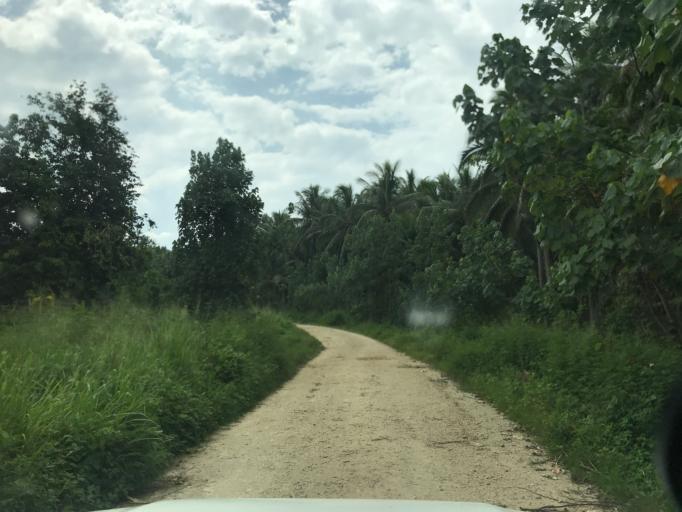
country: VU
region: Sanma
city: Port-Olry
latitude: -15.1745
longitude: 166.9529
